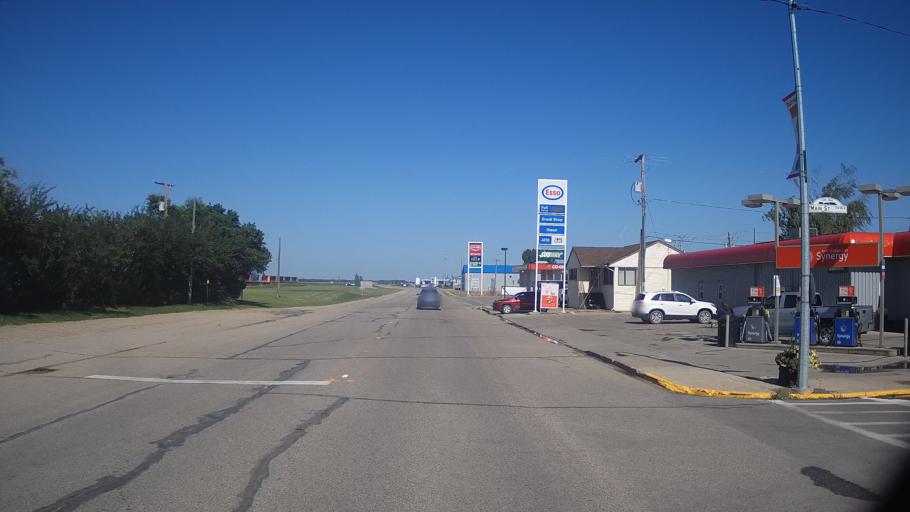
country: CA
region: Saskatchewan
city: Watrous
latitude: 51.6721
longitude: -105.4690
